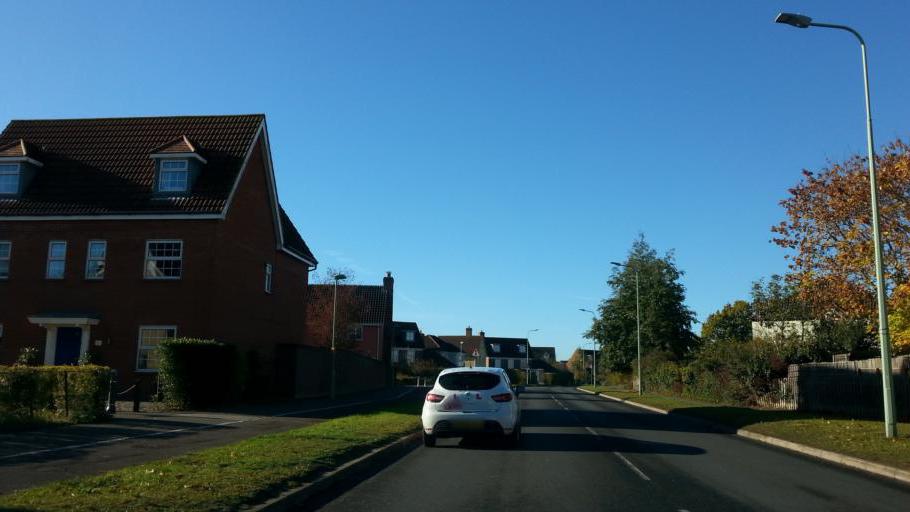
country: GB
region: England
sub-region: Suffolk
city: Kesgrave
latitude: 52.0605
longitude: 1.2470
